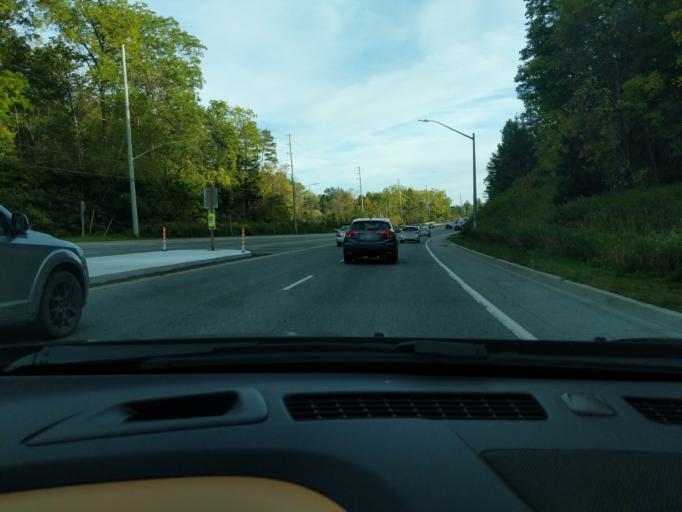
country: CA
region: Ontario
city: Newmarket
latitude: 44.0353
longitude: -79.4976
